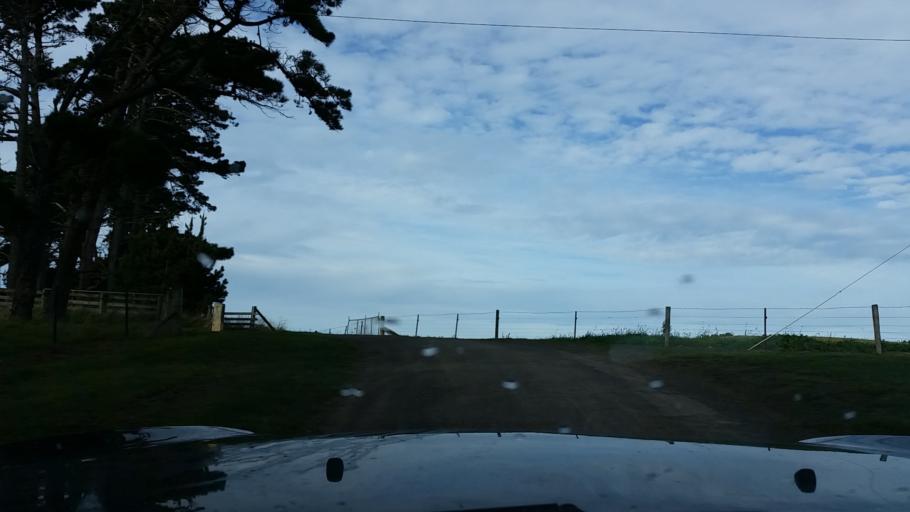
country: NZ
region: Marlborough
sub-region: Marlborough District
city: Blenheim
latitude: -41.6325
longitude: 174.1563
